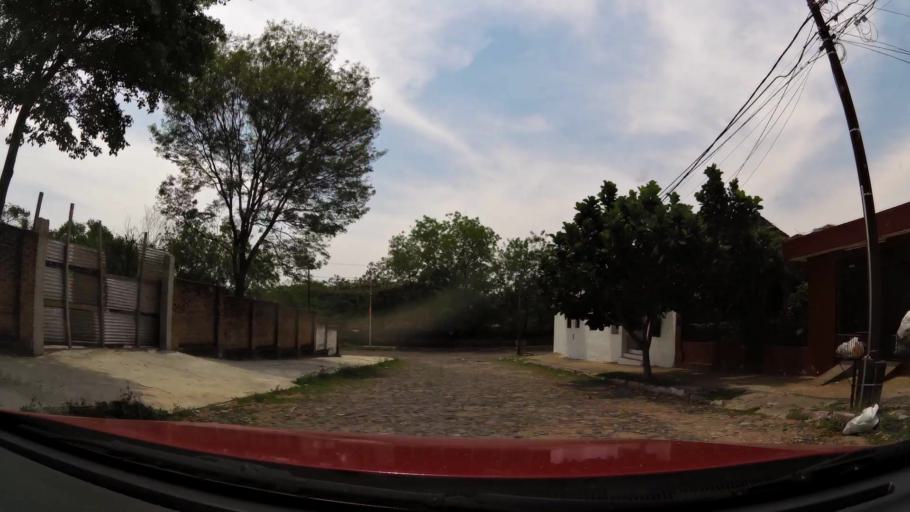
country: PY
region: Asuncion
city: Asuncion
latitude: -25.2683
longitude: -57.5952
